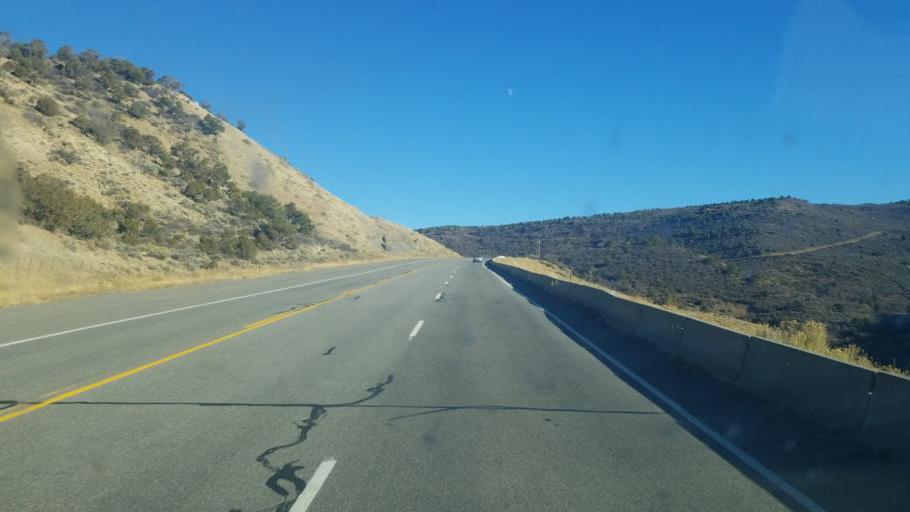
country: US
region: Colorado
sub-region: Montrose County
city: Montrose
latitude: 38.4605
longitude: -107.6795
